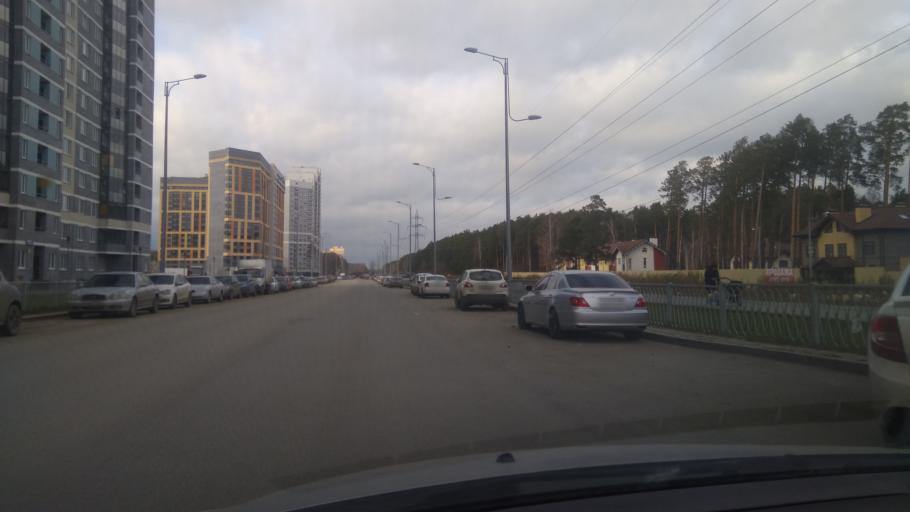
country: RU
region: Sverdlovsk
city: Sovkhoznyy
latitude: 56.7832
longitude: 60.5537
